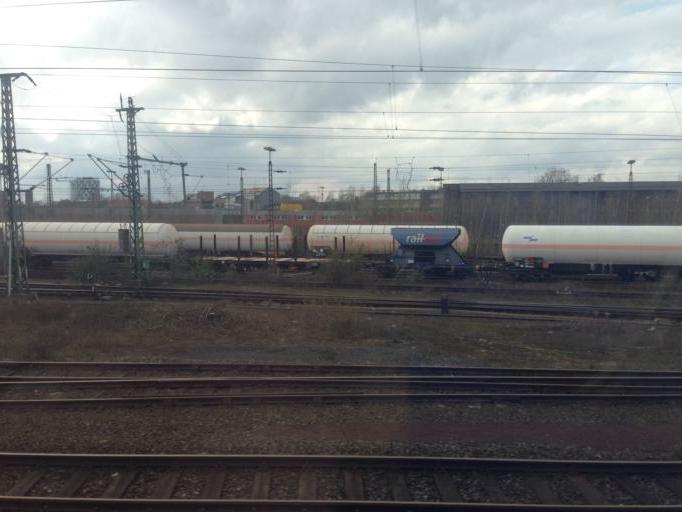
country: DE
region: North Rhine-Westphalia
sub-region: Regierungsbezirk Munster
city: Muenster
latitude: 51.9443
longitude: 7.6337
